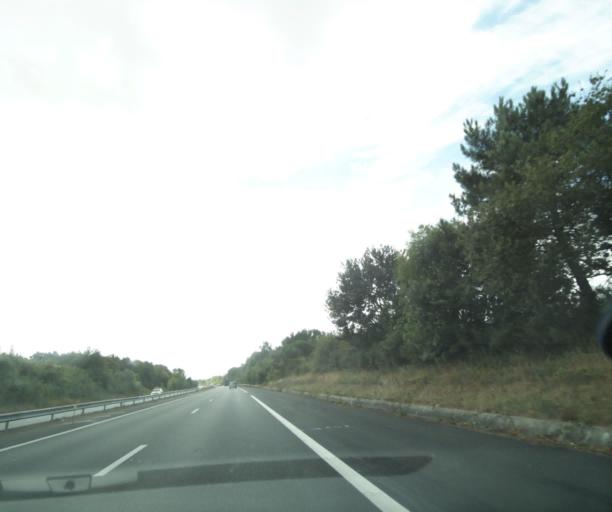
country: FR
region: Poitou-Charentes
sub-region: Departement de la Charente-Maritime
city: Thenac
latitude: 45.6510
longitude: -0.6331
